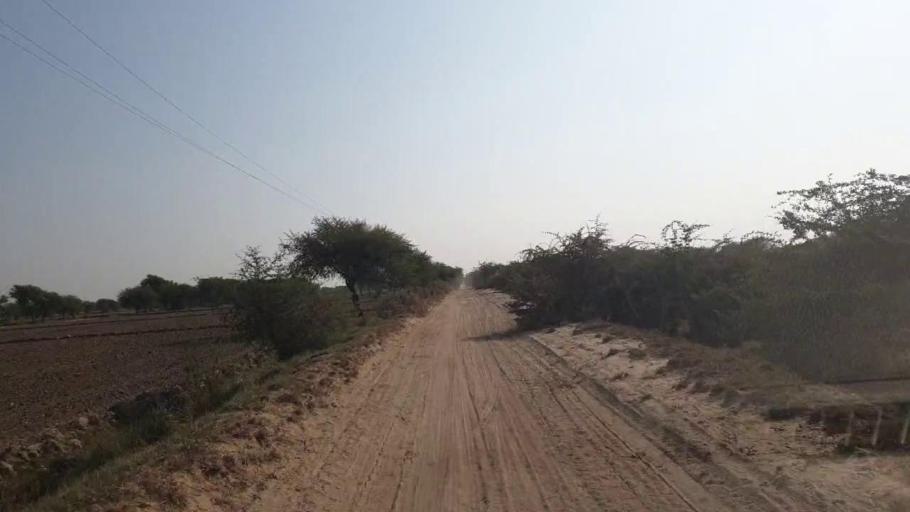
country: PK
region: Sindh
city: Kario
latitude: 24.8891
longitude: 68.6483
